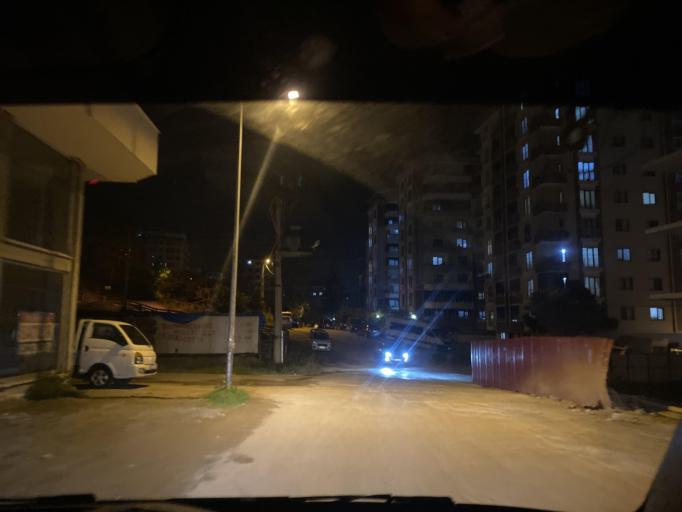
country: TR
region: Trabzon
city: Yomra
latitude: 40.9570
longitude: 39.8523
